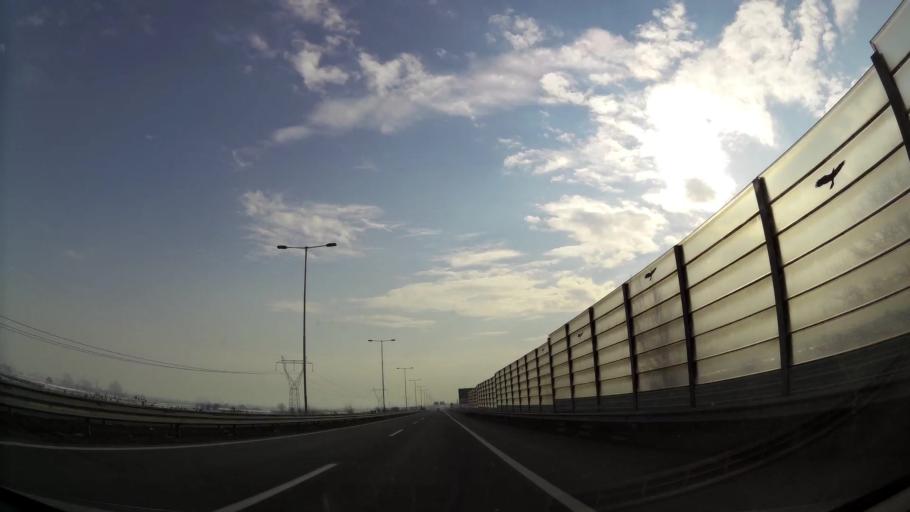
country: MK
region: Aracinovo
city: Arachinovo
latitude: 42.0261
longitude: 21.5306
